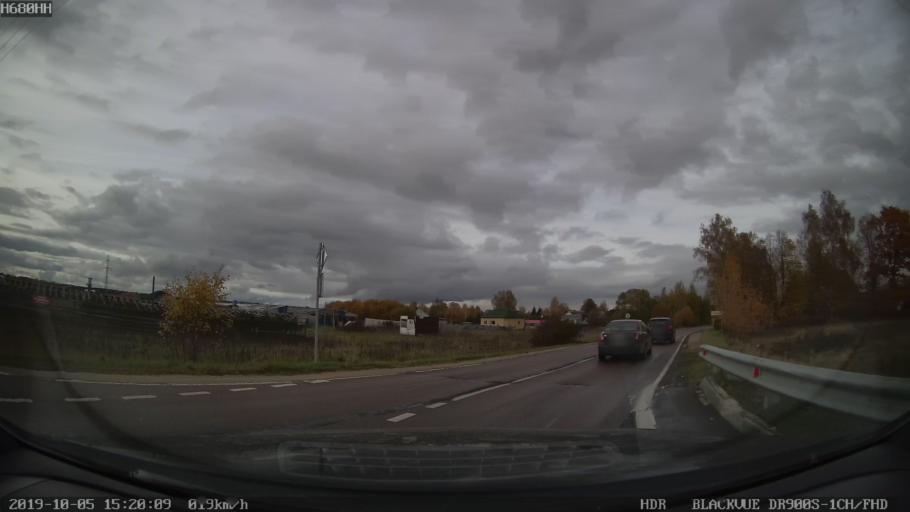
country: RU
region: Moskovskaya
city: Solnechnogorsk
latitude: 56.2215
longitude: 36.9048
